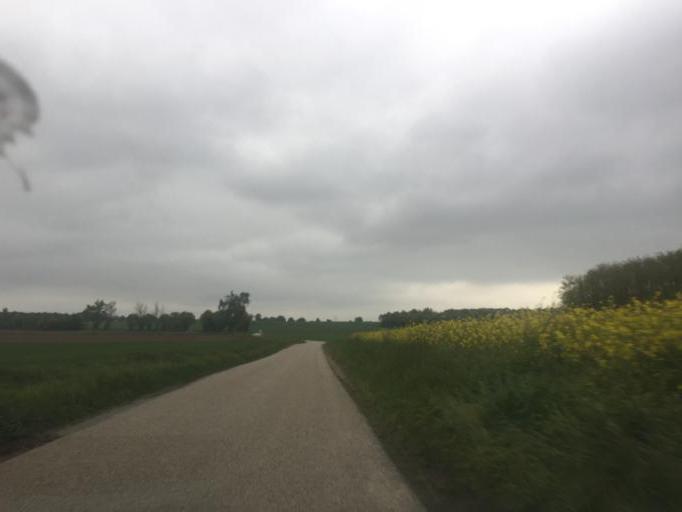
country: FR
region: Rhone-Alpes
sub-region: Departement de l'Ain
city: Tramoyes
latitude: 45.8809
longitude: 4.9751
